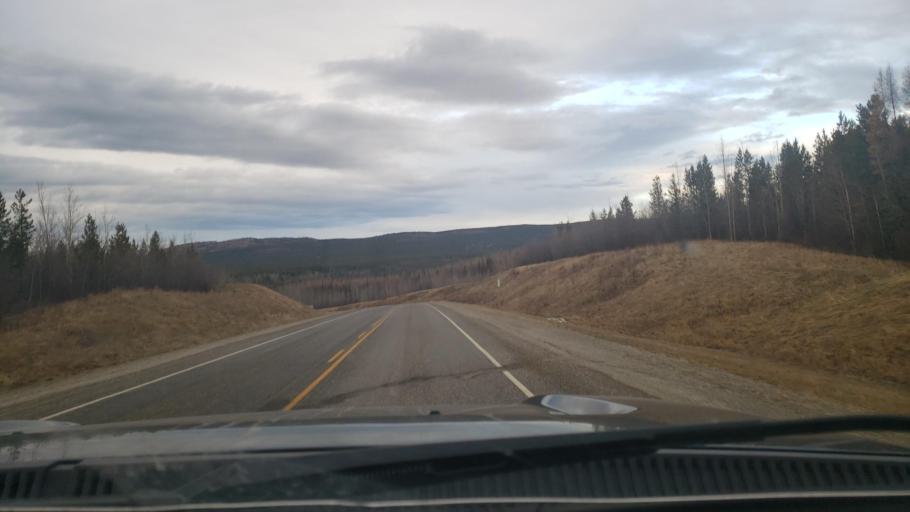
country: CA
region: Yukon
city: Watson Lake
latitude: 59.7861
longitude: -127.4567
